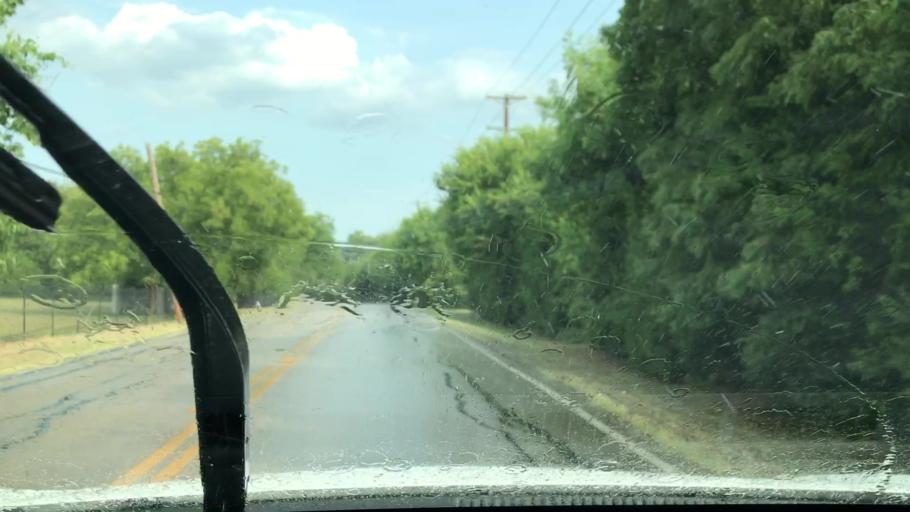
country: US
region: Texas
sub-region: Collin County
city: Wylie
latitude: 32.9536
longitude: -96.5234
